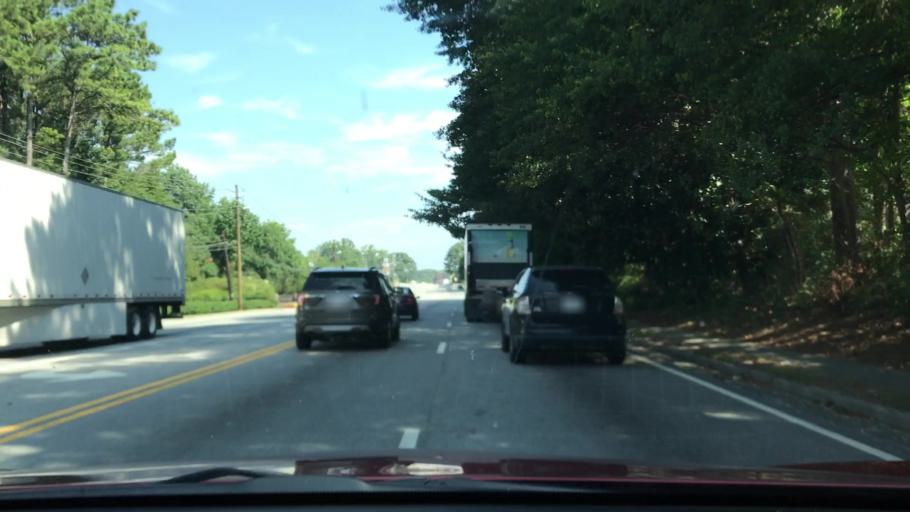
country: US
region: Georgia
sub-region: DeKalb County
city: Tucker
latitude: 33.8882
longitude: -84.1941
